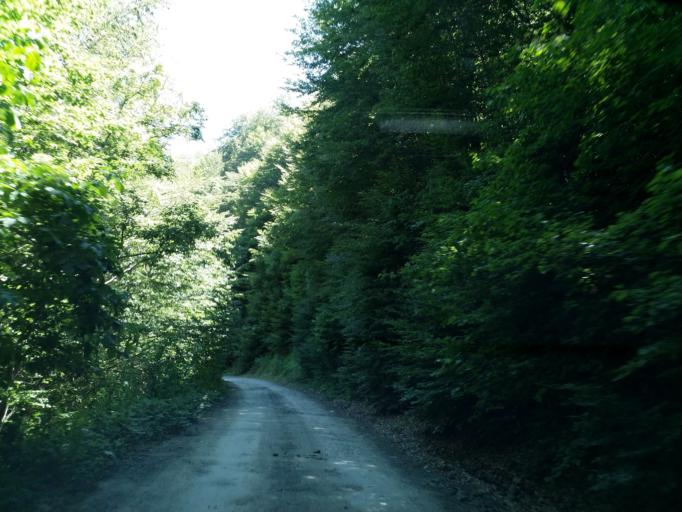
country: XK
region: Mitrovica
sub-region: Komuna e Leposaviqit
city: Leposaviq
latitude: 43.2760
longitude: 20.8701
